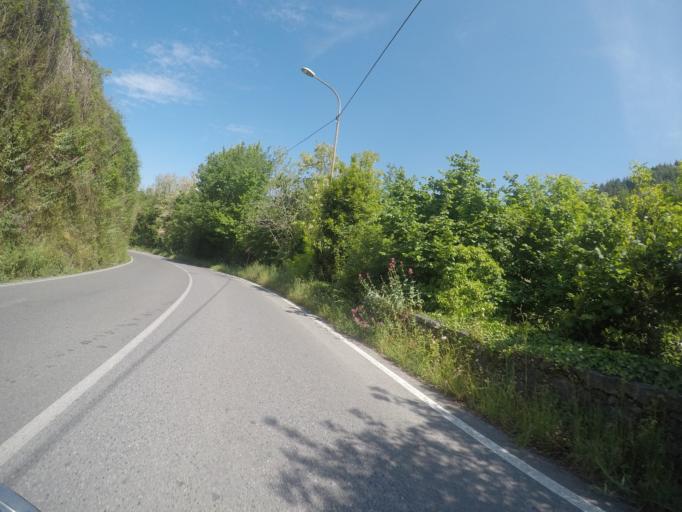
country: IT
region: Tuscany
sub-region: Provincia di Massa-Carrara
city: Massa
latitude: 44.0694
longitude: 10.1090
